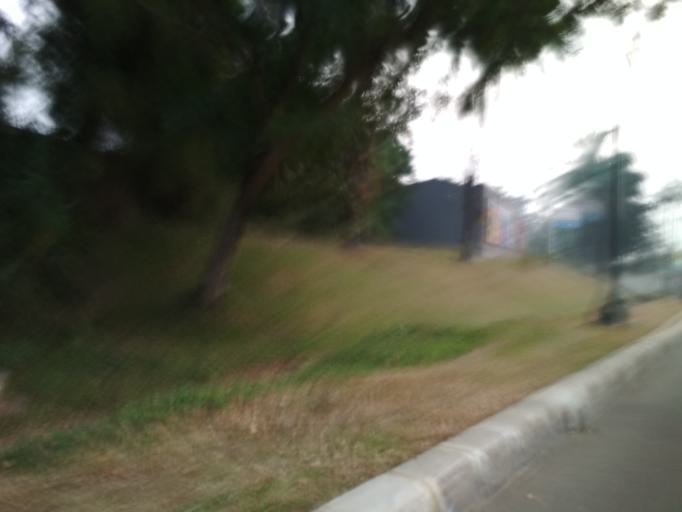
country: ID
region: West Java
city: Caringin
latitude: -6.6621
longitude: 106.8372
